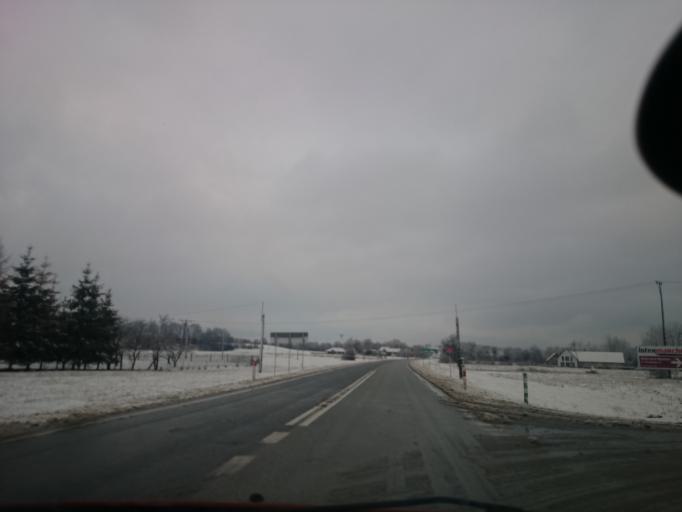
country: PL
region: Lower Silesian Voivodeship
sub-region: Powiat klodzki
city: Bystrzyca Klodzka
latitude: 50.3167
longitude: 16.6606
